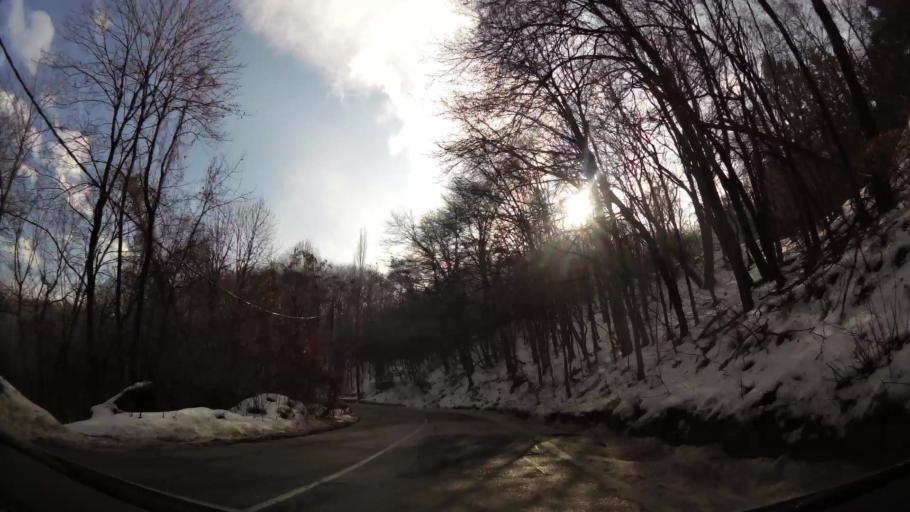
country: BG
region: Sofia-Capital
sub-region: Stolichna Obshtina
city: Sofia
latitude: 42.6467
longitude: 23.2478
